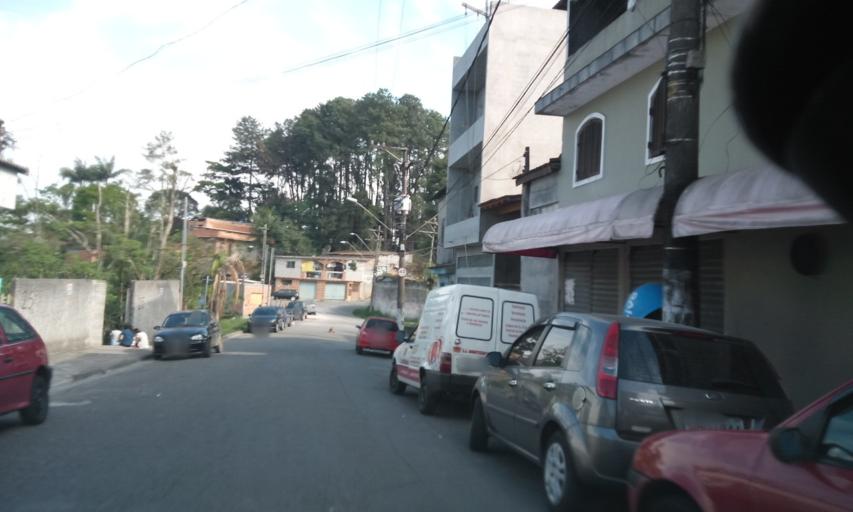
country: BR
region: Sao Paulo
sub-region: Sao Bernardo Do Campo
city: Sao Bernardo do Campo
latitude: -23.8021
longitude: -46.5410
